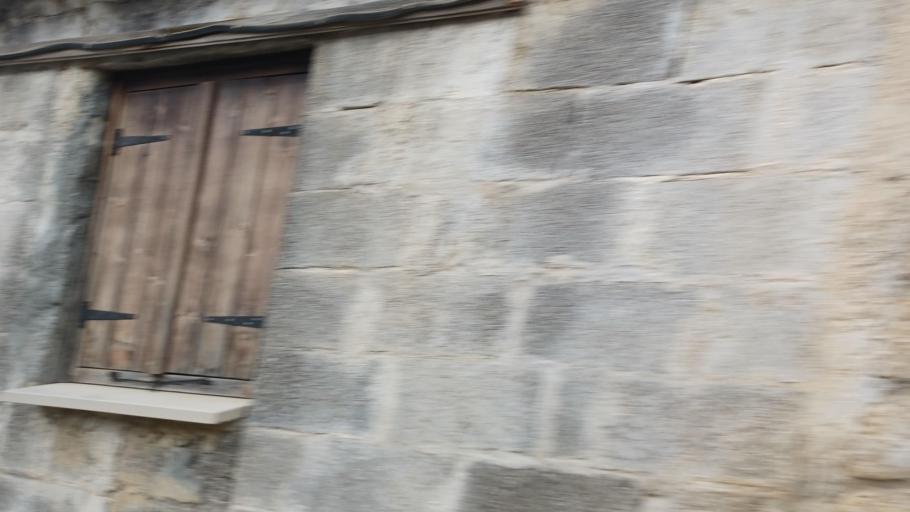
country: CY
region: Limassol
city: Pachna
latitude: 34.7404
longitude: 32.7342
